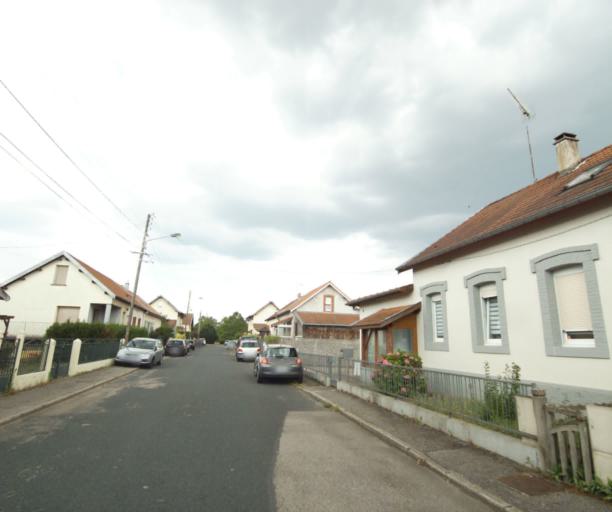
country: FR
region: Lorraine
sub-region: Departement de Meurthe-et-Moselle
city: Chanteheux
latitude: 48.5864
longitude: 6.5168
